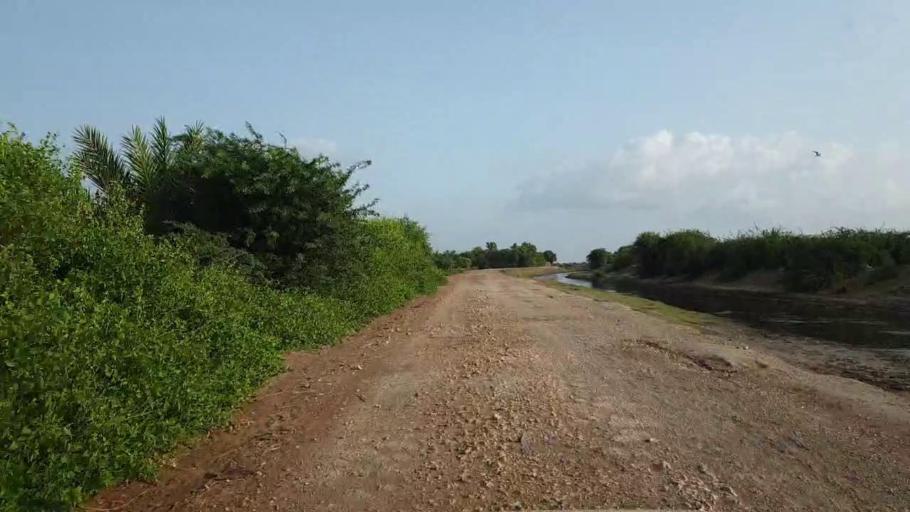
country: PK
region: Sindh
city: Kario
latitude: 24.8388
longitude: 68.6523
